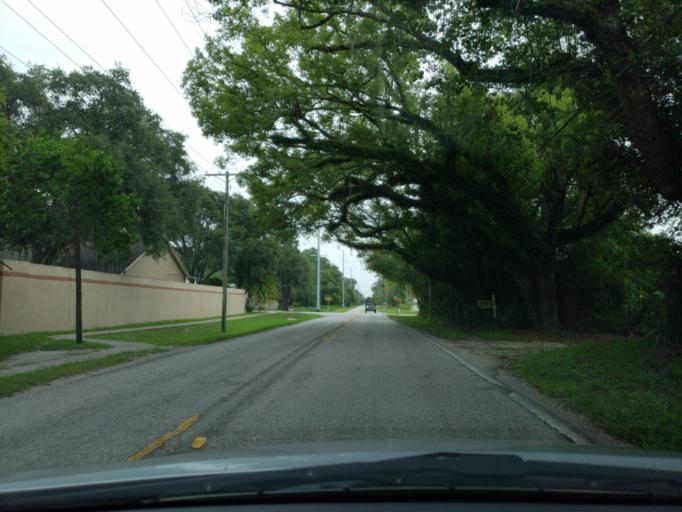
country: US
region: Florida
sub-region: Hillsborough County
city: Lutz
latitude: 28.1424
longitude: -82.4580
